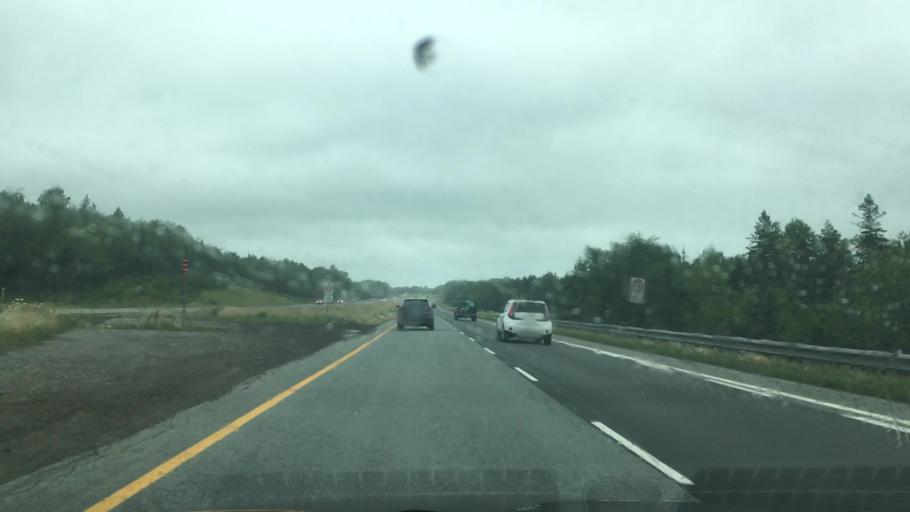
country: CA
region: Nova Scotia
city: Truro
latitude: 45.2540
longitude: -63.2920
